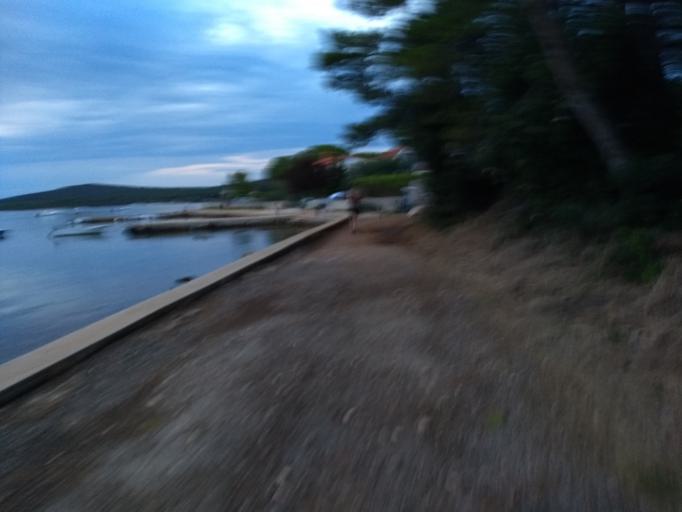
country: HR
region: Zadarska
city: Ugljan
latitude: 44.1351
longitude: 15.0702
